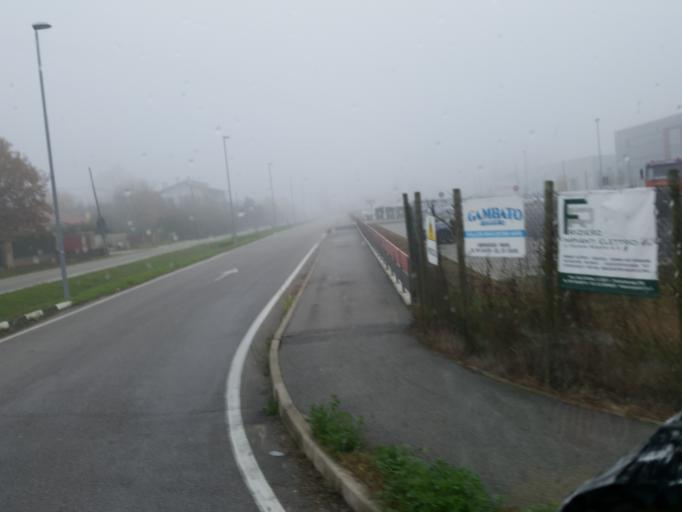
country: IT
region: Veneto
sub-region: Provincia di Padova
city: Borgoricco-San Michele delle Badesse-Sant'Eufemia
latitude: 45.5402
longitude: 11.9495
